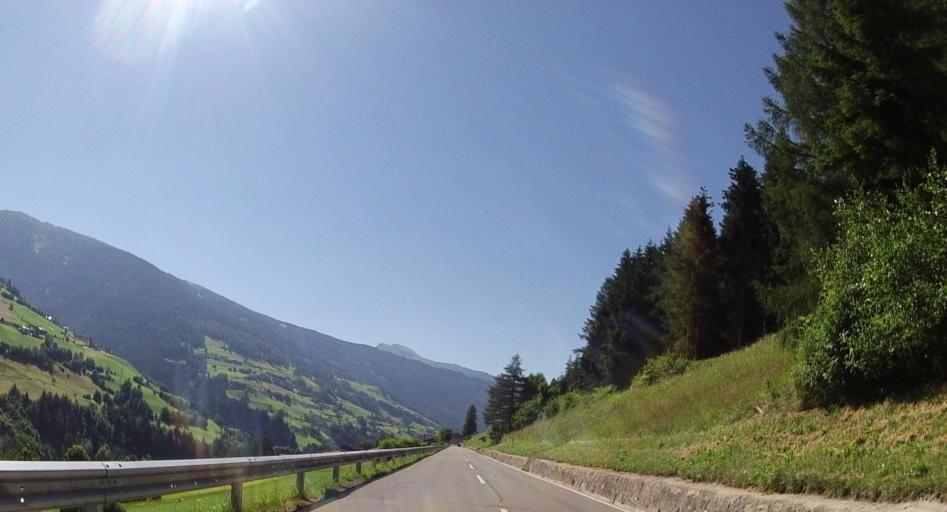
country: AT
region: Tyrol
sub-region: Politischer Bezirk Innsbruck Land
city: Ellbogen
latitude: 47.1690
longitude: 11.4313
